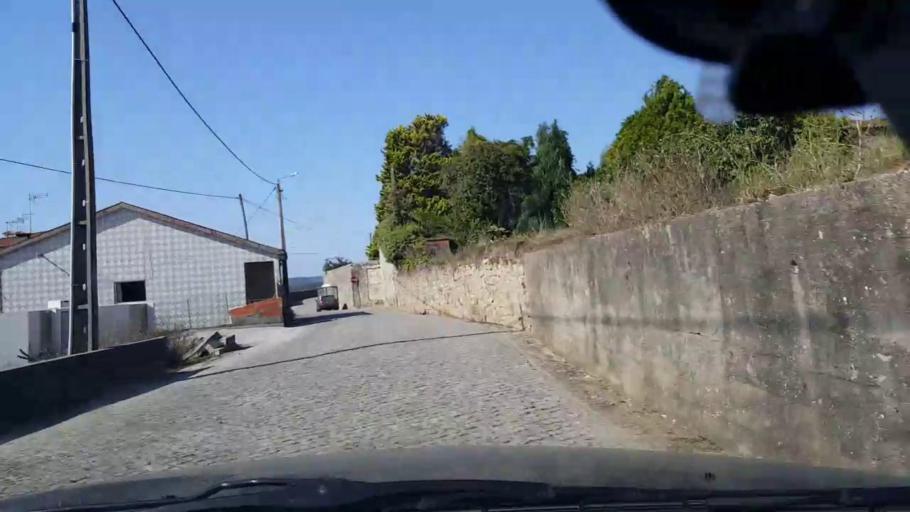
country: PT
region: Porto
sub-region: Vila do Conde
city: Arvore
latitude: 41.3612
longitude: -8.6984
